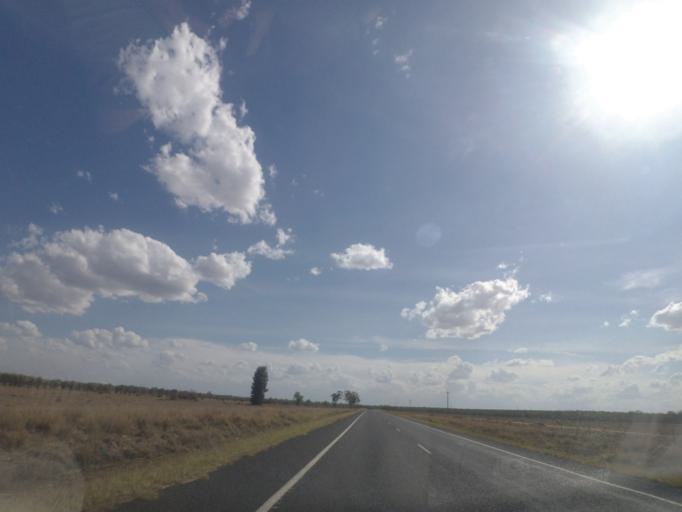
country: AU
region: New South Wales
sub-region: Moree Plains
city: Boggabilla
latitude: -28.5246
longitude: 150.9037
